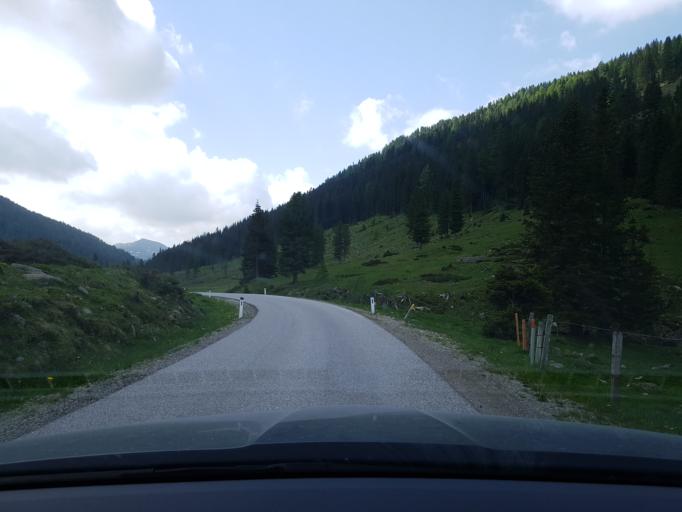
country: AT
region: Salzburg
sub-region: Politischer Bezirk Tamsweg
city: Thomatal
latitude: 47.0210
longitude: 13.7632
